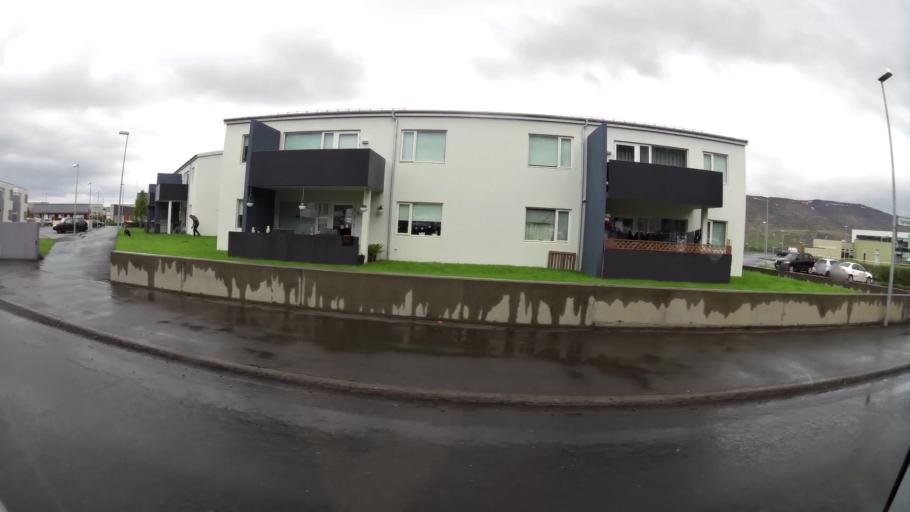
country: IS
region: Northeast
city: Akureyri
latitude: 65.6656
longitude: -18.1022
